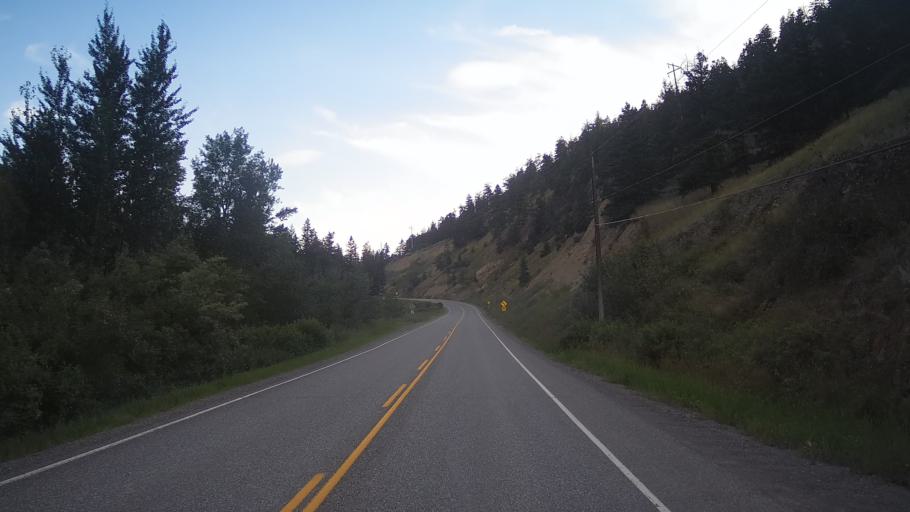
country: CA
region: British Columbia
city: Cache Creek
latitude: 50.8680
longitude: -121.5245
